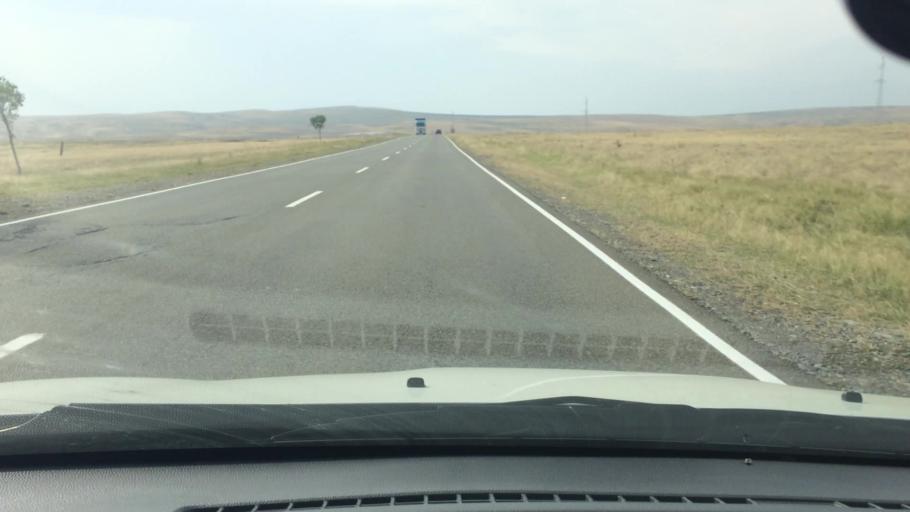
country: GE
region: Kvemo Kartli
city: Rust'avi
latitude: 41.5339
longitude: 44.9501
